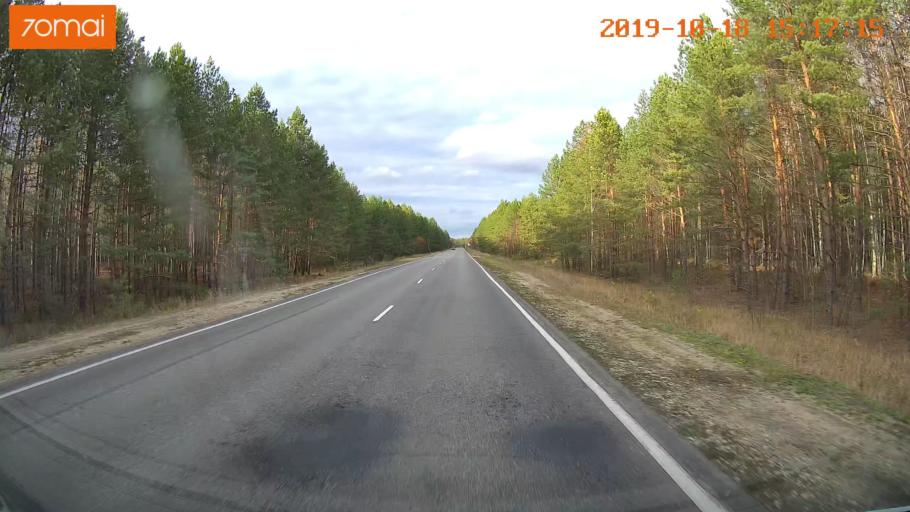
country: RU
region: Vladimir
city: Anopino
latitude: 55.6469
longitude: 40.7262
